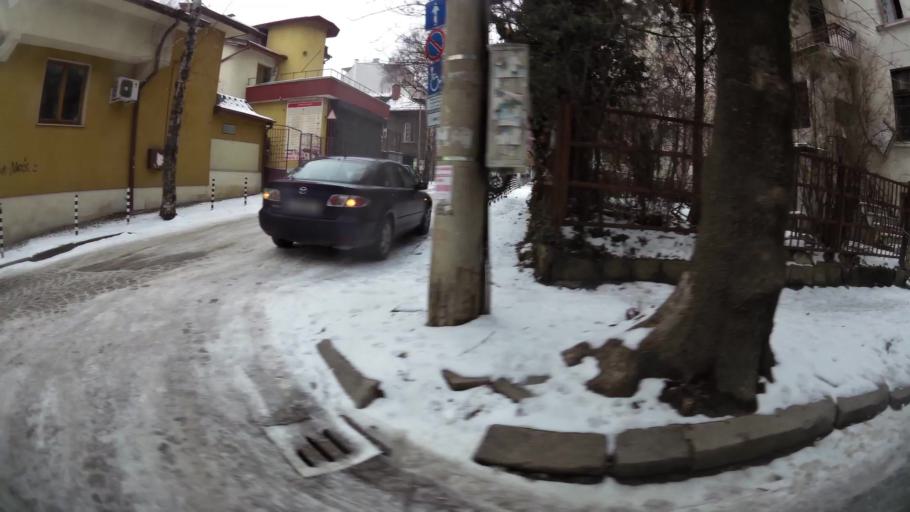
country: BG
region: Sofia-Capital
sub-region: Stolichna Obshtina
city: Sofia
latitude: 42.7075
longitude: 23.3167
